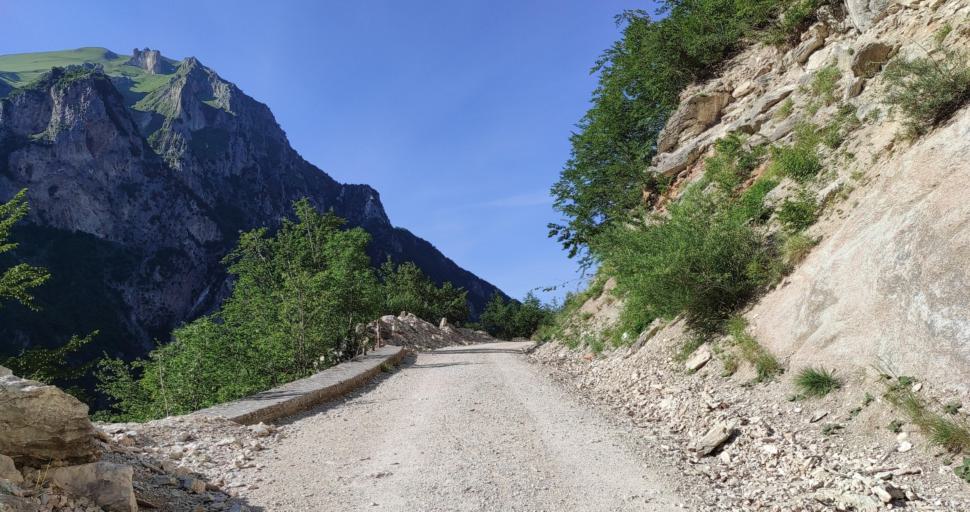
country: IT
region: The Marches
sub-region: Provincia di Ascoli Piceno
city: Montemonaco
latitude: 42.9237
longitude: 13.2806
